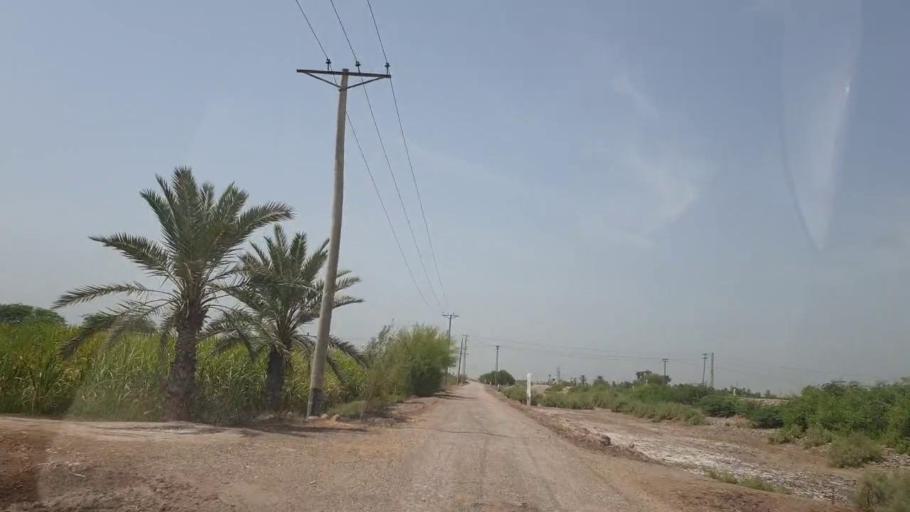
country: PK
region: Sindh
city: Gambat
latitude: 27.3209
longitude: 68.5366
